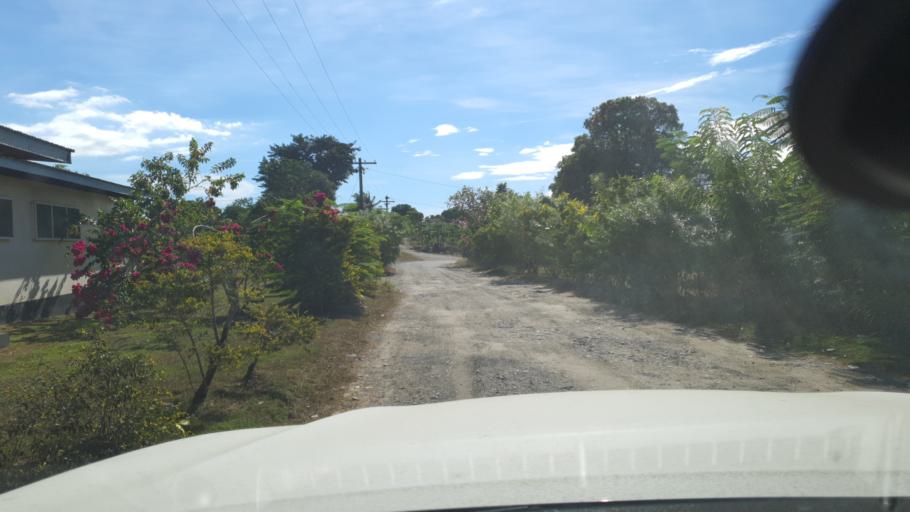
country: SB
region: Guadalcanal
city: Honiara
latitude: -9.4306
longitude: 160.0173
